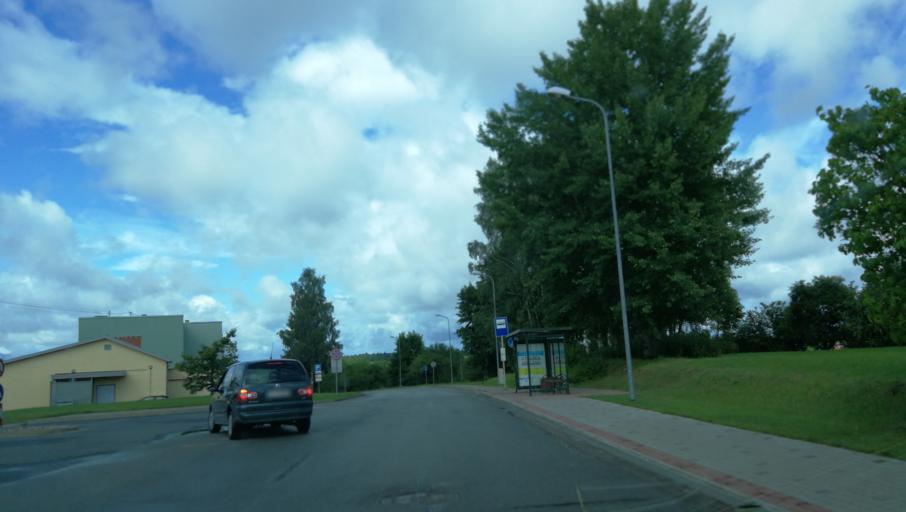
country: LV
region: Cesu Rajons
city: Cesis
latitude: 57.3153
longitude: 25.2591
